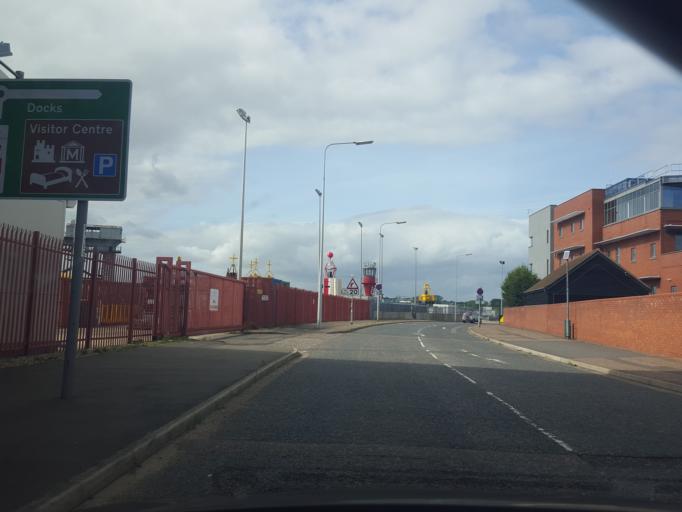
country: GB
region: England
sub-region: Essex
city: Harwich
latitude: 51.9461
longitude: 1.2855
